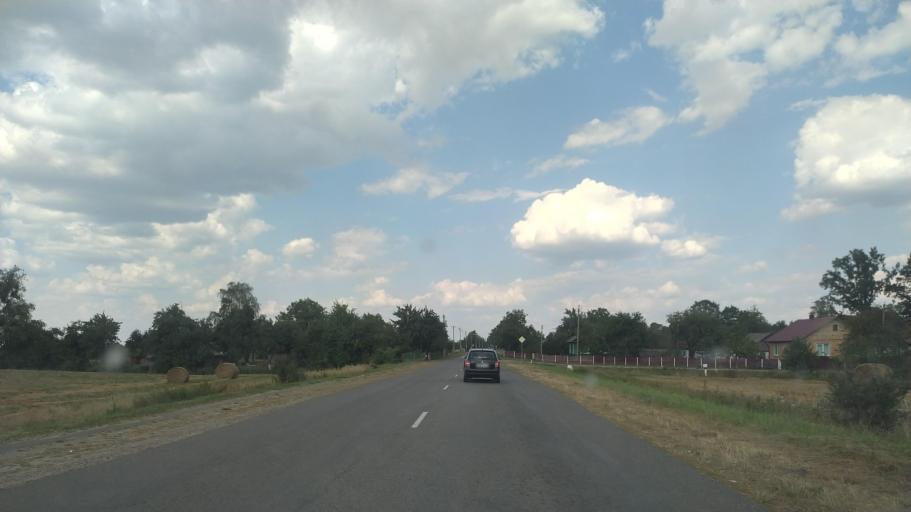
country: BY
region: Brest
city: Drahichyn
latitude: 52.1112
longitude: 25.1149
